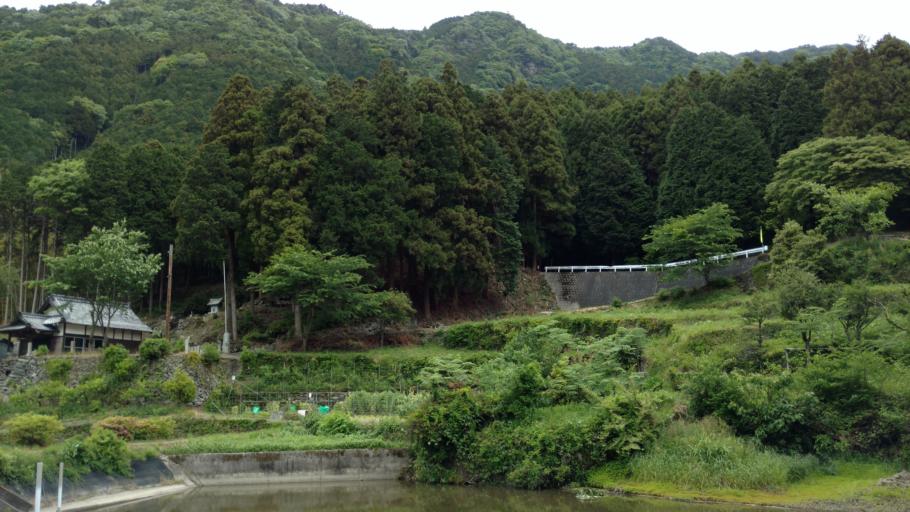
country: JP
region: Ehime
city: Saijo
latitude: 33.8661
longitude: 133.1984
